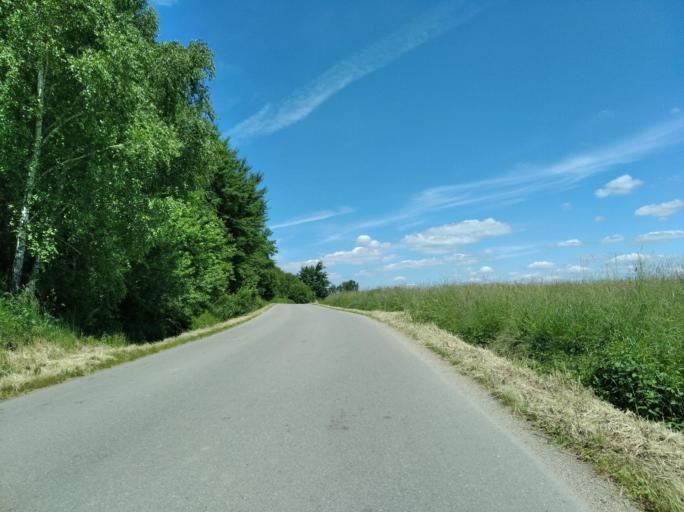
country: PL
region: Subcarpathian Voivodeship
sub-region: Powiat krosnienski
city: Wojaszowka
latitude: 49.7692
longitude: 21.6379
